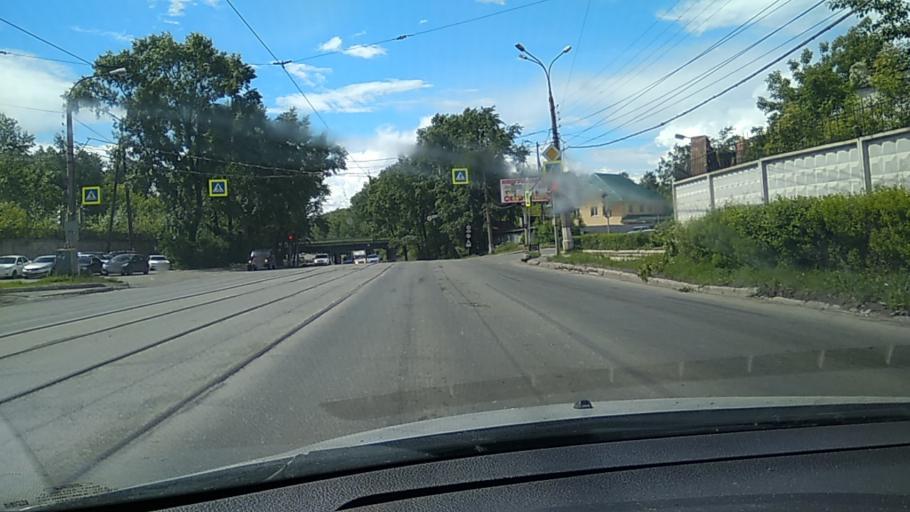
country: RU
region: Sverdlovsk
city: Nizhniy Tagil
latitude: 57.9299
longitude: 60.0028
